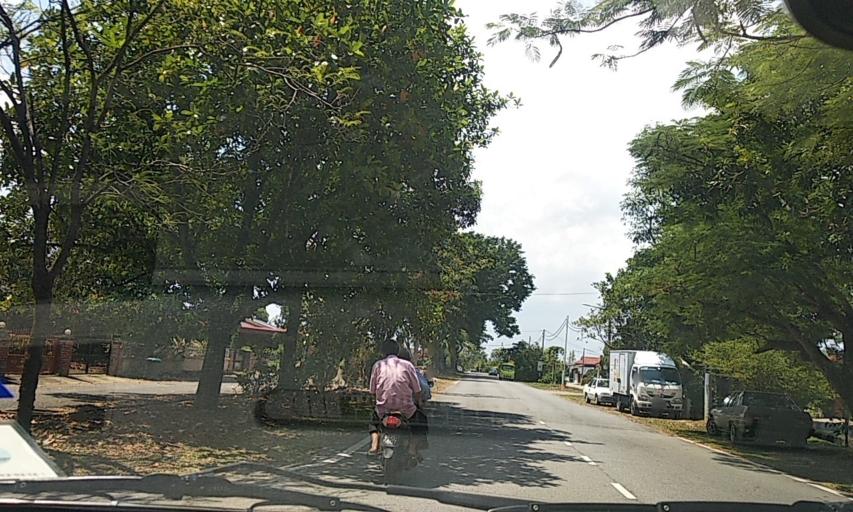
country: MY
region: Kedah
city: Sungai Petani
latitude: 5.6337
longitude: 100.4692
